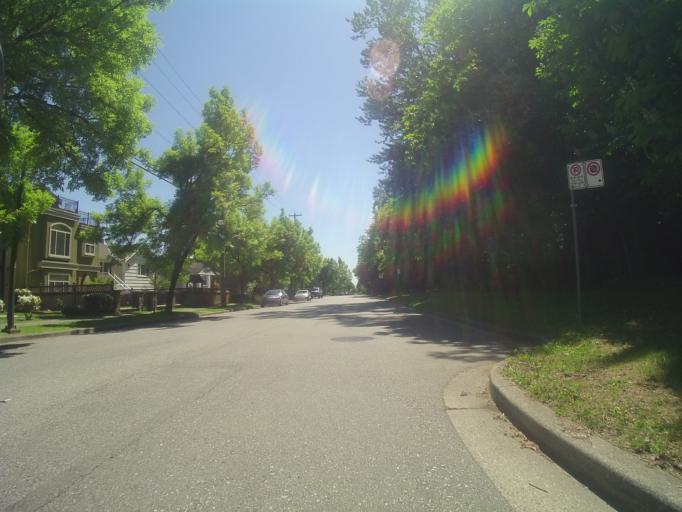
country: CA
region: British Columbia
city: Vancouver
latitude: 49.2229
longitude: -123.1061
